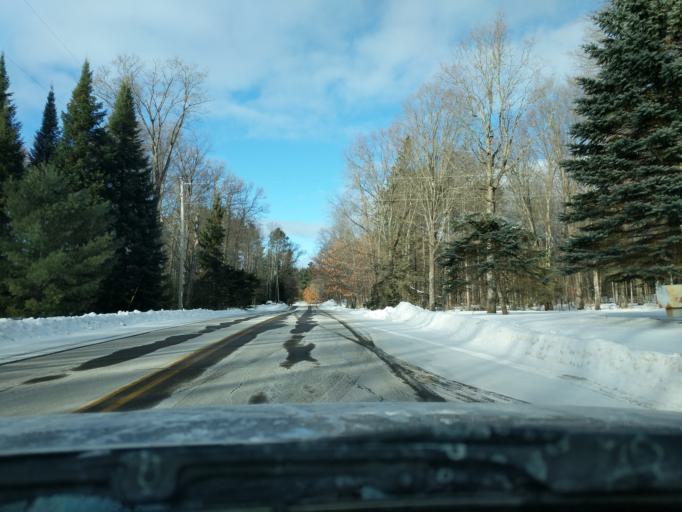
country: US
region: Wisconsin
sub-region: Vilas County
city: Eagle River
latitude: 45.7863
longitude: -89.0784
